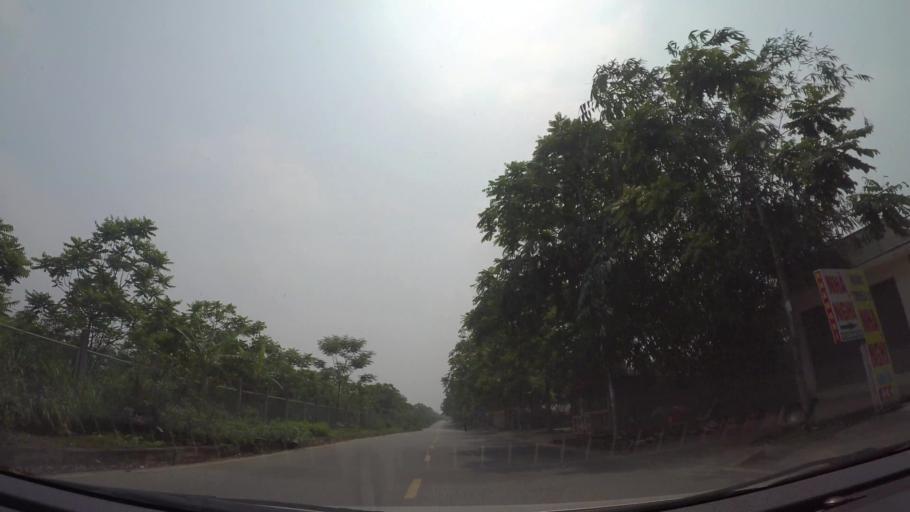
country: VN
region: Ha Noi
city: Lien Quan
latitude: 20.9900
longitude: 105.5451
